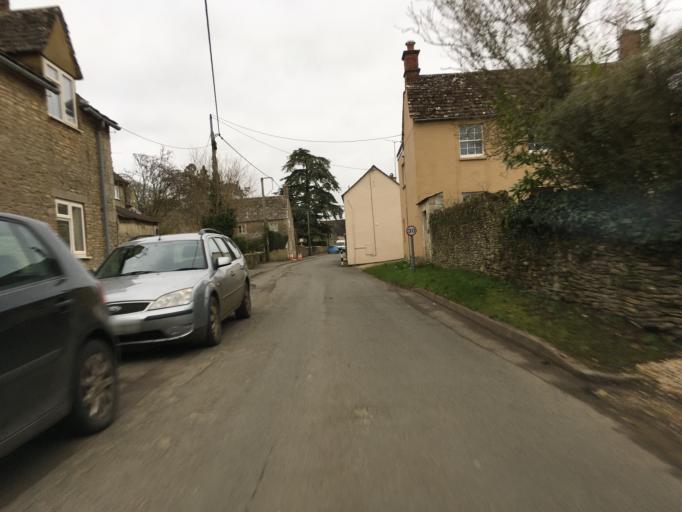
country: GB
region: England
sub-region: Wiltshire
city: Cricklade
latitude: 51.7040
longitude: -1.8575
